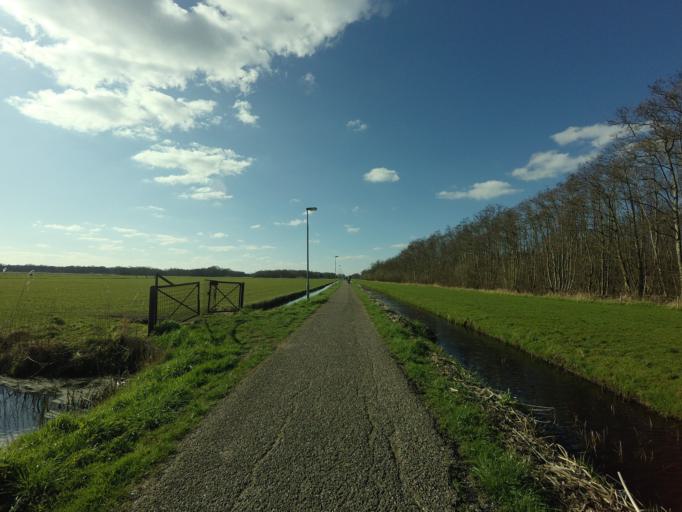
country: NL
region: North Holland
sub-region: Gemeente Wijdemeren
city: Kortenhoef
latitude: 52.2621
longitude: 5.1153
